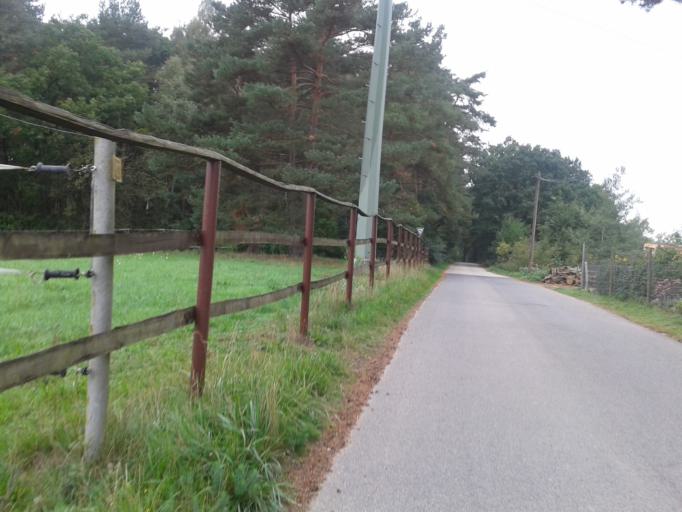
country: DE
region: Bavaria
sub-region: Upper Franconia
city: Gundelsheim
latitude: 49.9271
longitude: 10.9031
